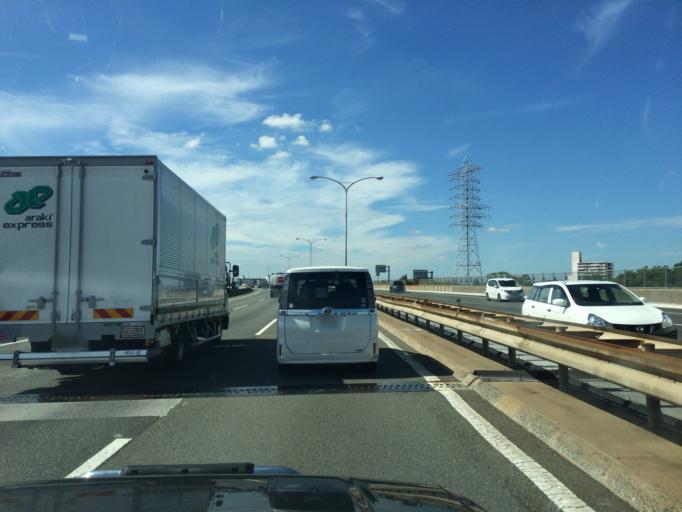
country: JP
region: Osaka
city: Yao
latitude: 34.6304
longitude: 135.5818
